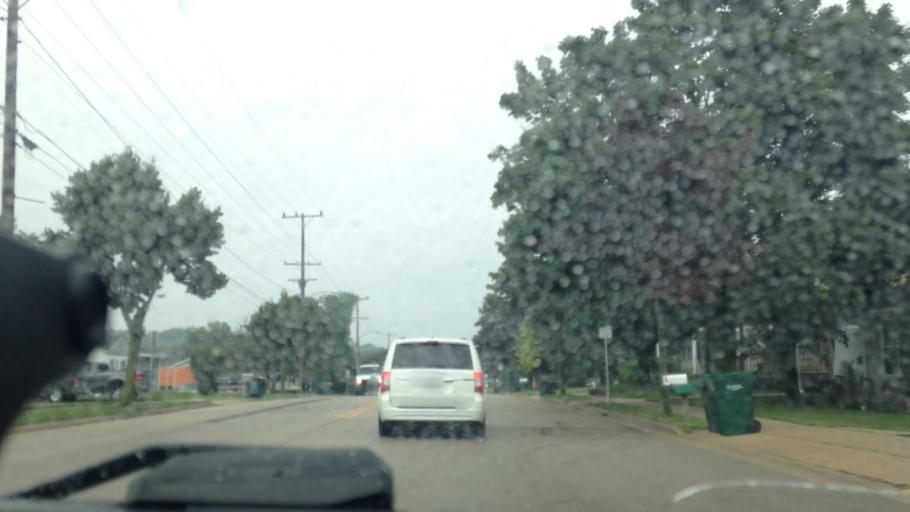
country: US
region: Wisconsin
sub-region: Washington County
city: Slinger
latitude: 43.3324
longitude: -88.2827
